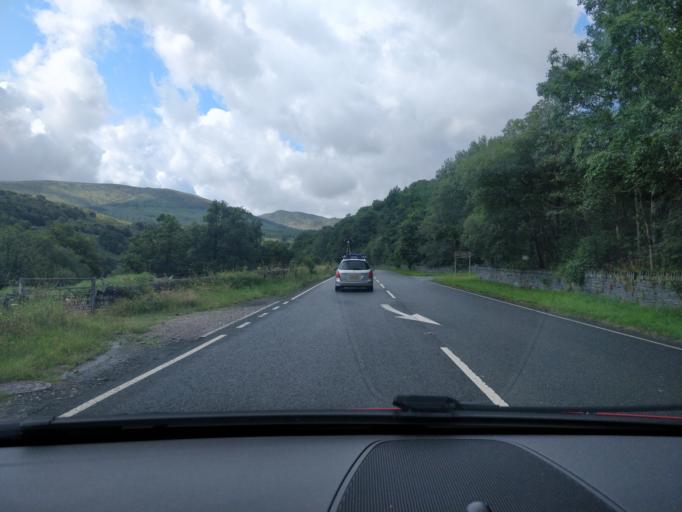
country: GB
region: Wales
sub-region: Gwynedd
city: Blaenau-Ffestiniog
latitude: 53.0521
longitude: -3.9062
